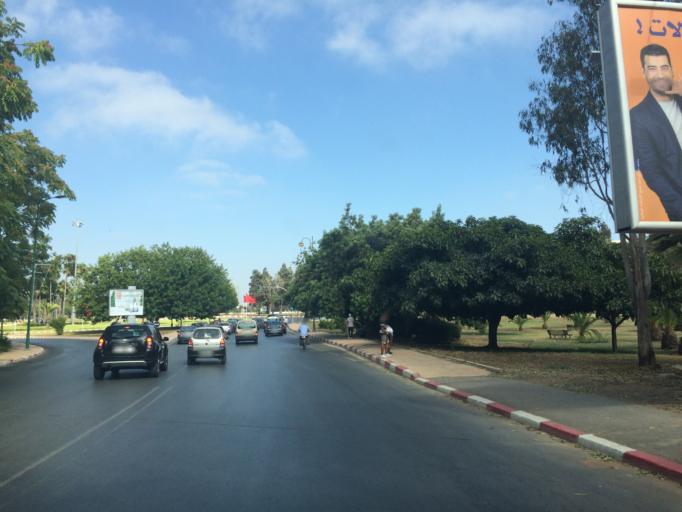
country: MA
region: Rabat-Sale-Zemmour-Zaer
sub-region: Rabat
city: Rabat
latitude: 33.9931
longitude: -6.8406
